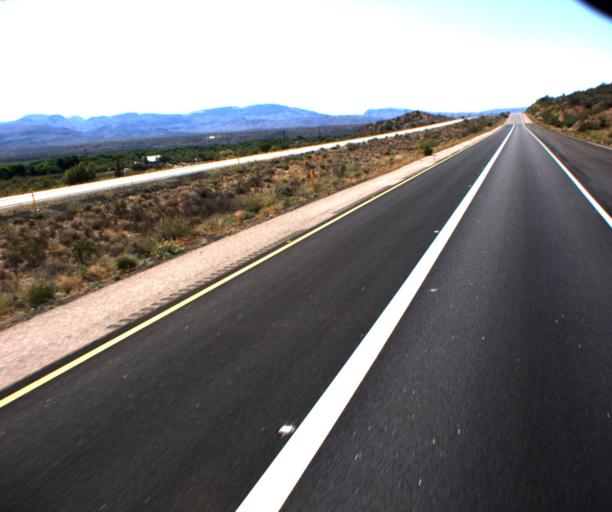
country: US
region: Arizona
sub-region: Yavapai County
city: Bagdad
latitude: 34.6847
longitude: -113.5993
